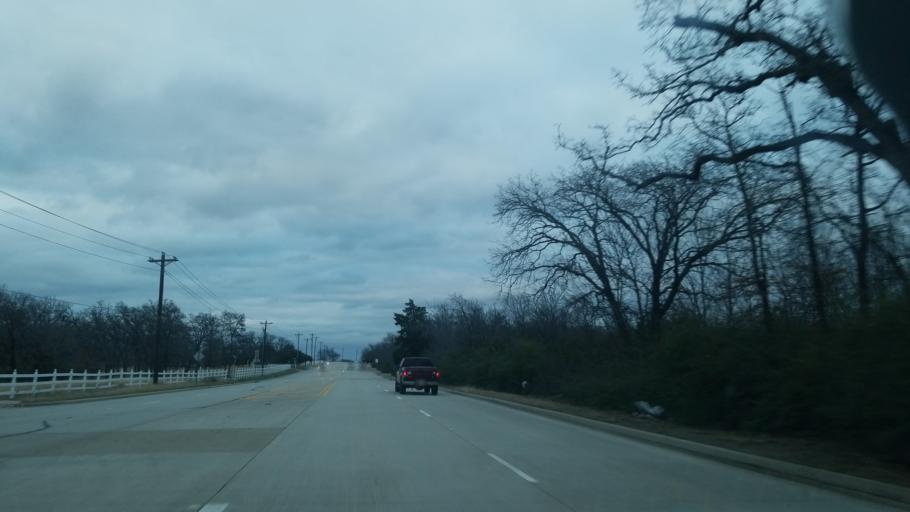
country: US
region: Texas
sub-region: Denton County
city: Lake Dallas
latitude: 33.1414
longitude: -96.9845
